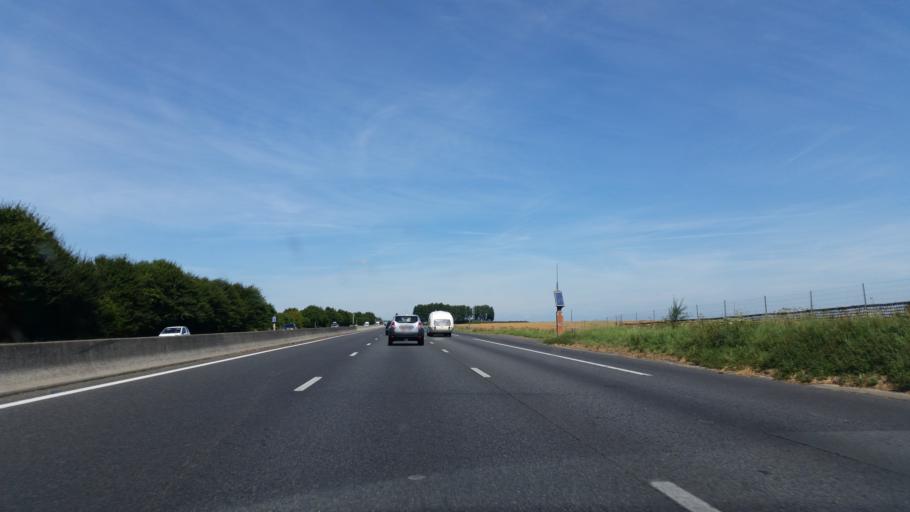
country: FR
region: Nord-Pas-de-Calais
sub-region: Departement du Pas-de-Calais
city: Vaulx-Vraucourt
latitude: 50.1515
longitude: 2.8731
